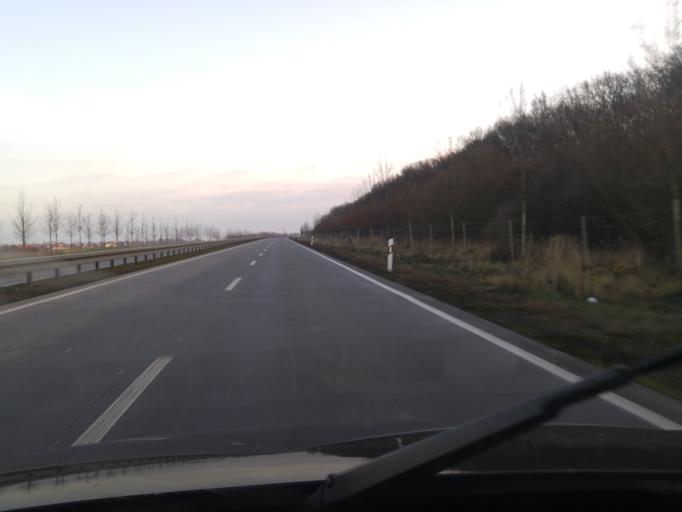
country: DE
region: Saxony
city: Rackwitz
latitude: 51.4087
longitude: 12.3215
